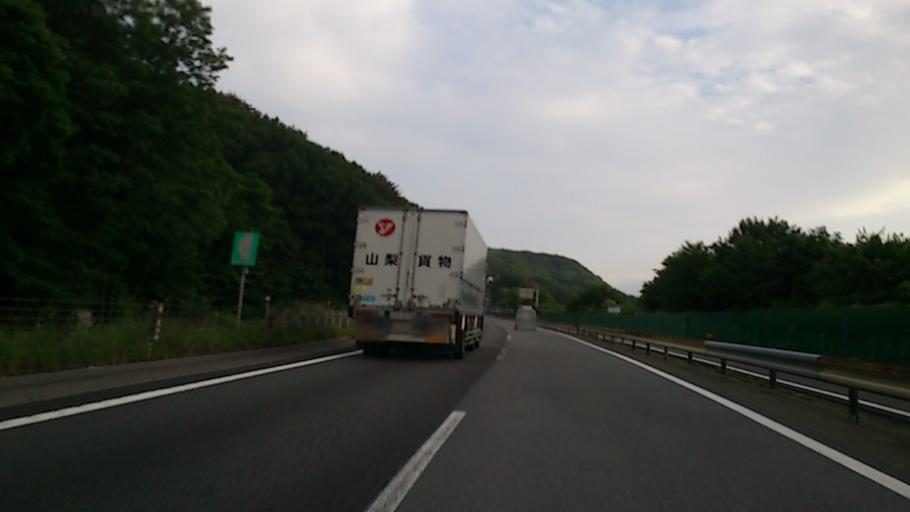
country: JP
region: Nagano
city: Okaya
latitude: 36.0449
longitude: 138.0304
